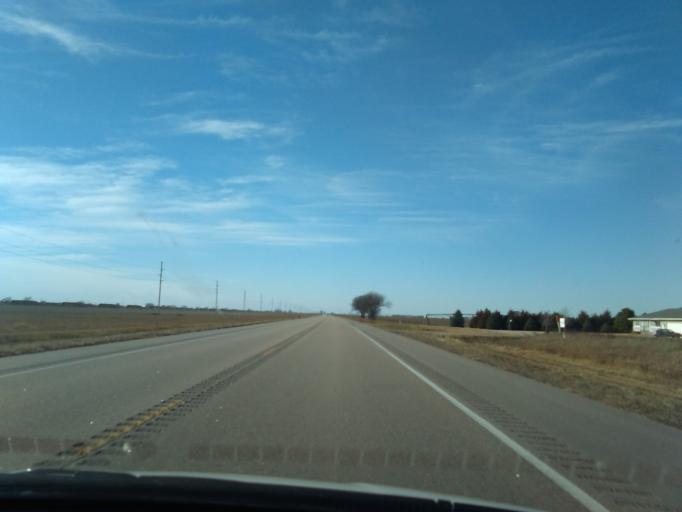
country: US
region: Nebraska
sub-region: Clay County
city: Harvard
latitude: 40.5828
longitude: -98.1729
